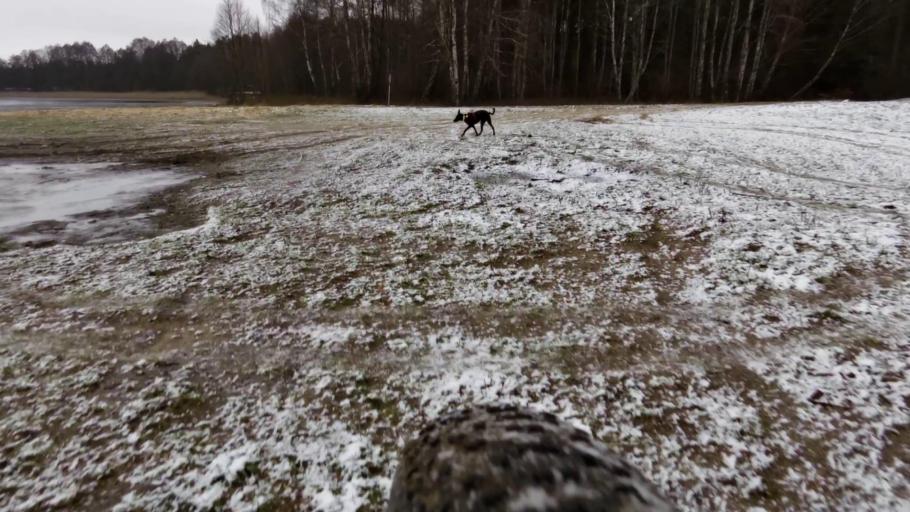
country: PL
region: West Pomeranian Voivodeship
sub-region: Powiat walecki
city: Miroslawiec
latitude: 53.3227
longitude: 16.0852
